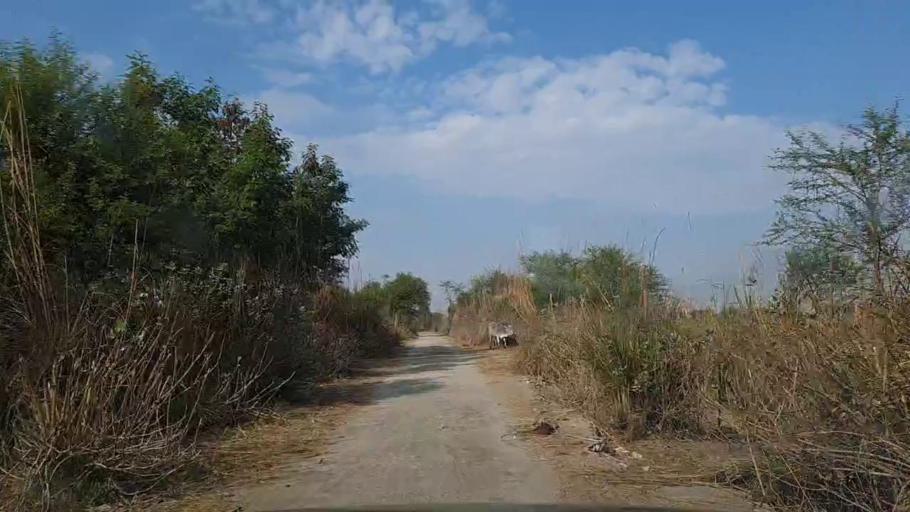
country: PK
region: Sindh
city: Sanghar
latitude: 26.2571
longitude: 69.0097
